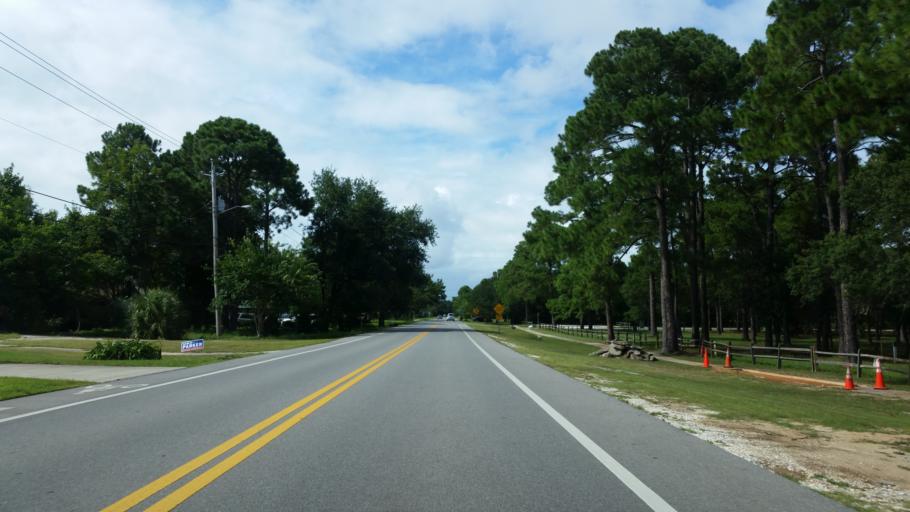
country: US
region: Florida
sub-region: Santa Rosa County
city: Gulf Breeze
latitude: 30.3554
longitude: -87.1794
